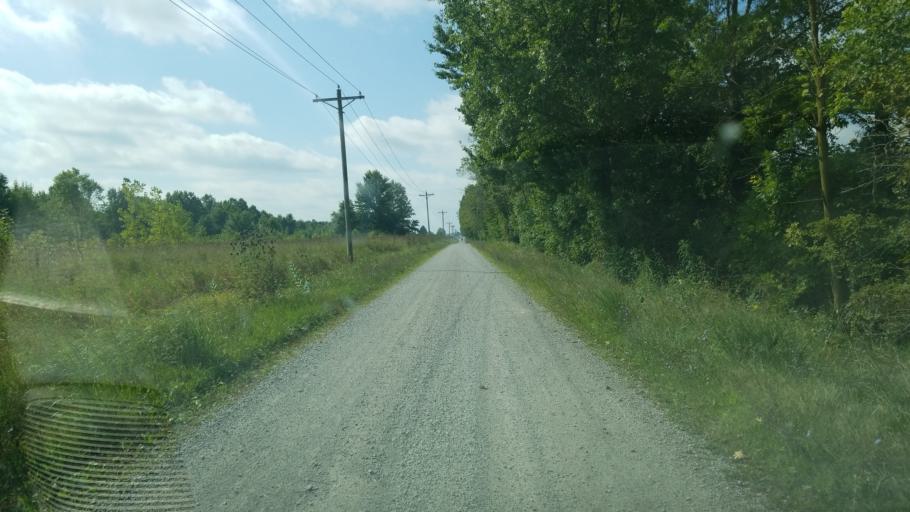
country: US
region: Ohio
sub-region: Wyandot County
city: Upper Sandusky
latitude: 40.7066
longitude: -83.3623
